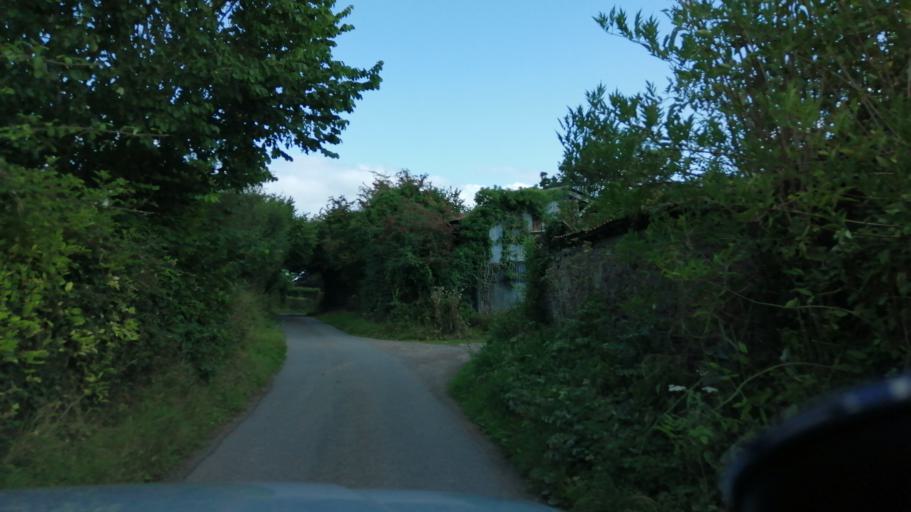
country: GB
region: England
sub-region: Herefordshire
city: Yazor
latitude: 52.1185
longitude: -2.9081
